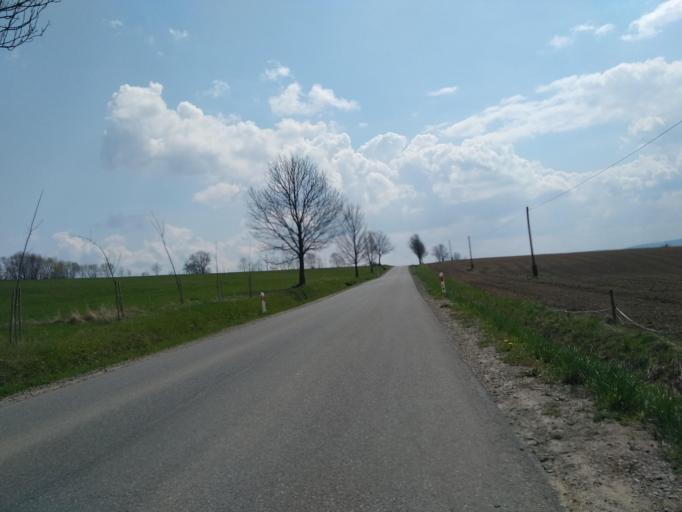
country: PL
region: Subcarpathian Voivodeship
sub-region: Powiat sanocki
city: Bukowsko
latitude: 49.4975
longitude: 22.0406
